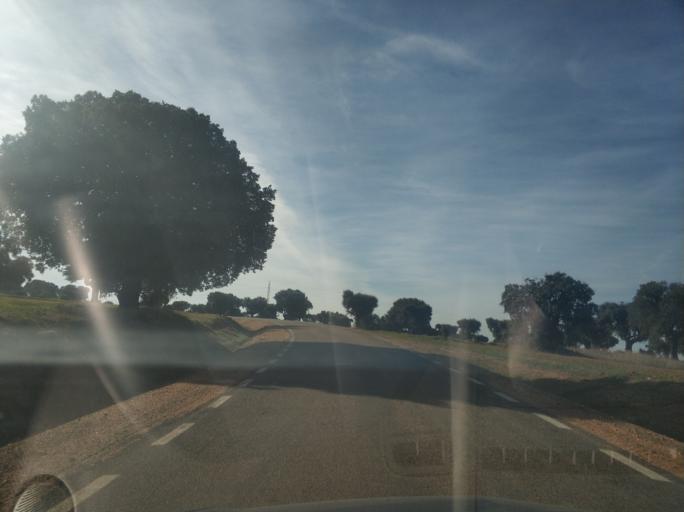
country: ES
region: Castille and Leon
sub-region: Provincia de Salamanca
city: Parada de Arriba
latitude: 41.0004
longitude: -5.8133
